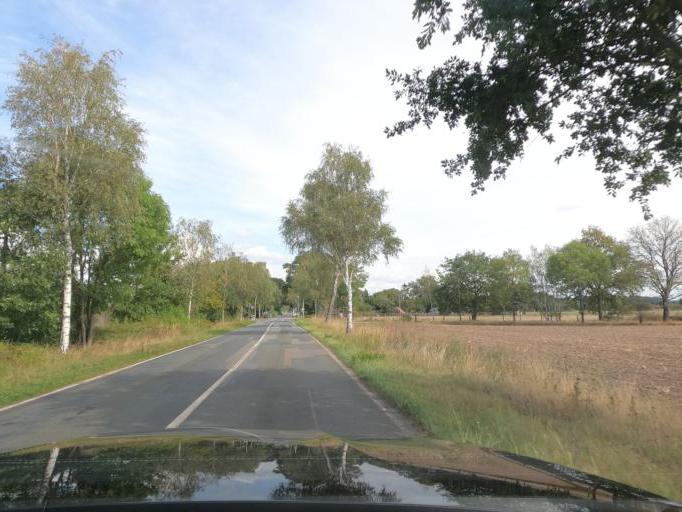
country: DE
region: Lower Saxony
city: Burgdorf
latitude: 52.4613
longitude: 9.9598
